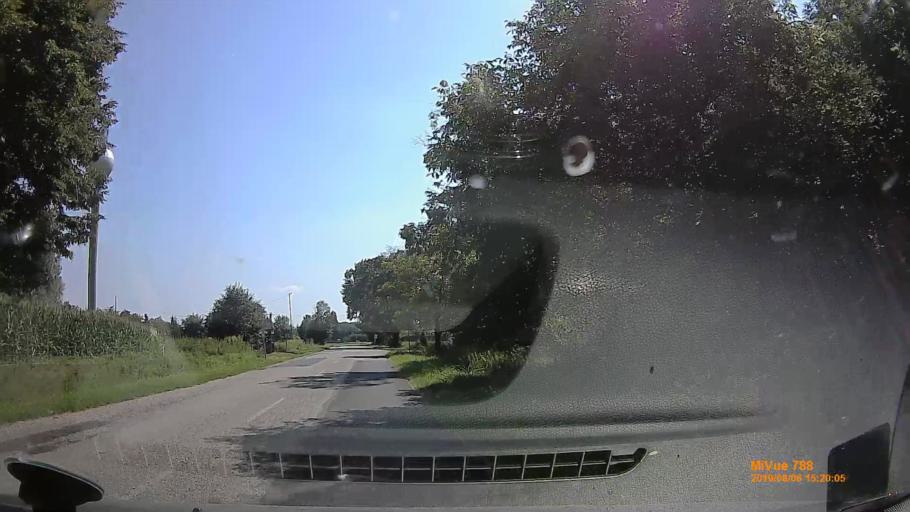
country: HR
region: Koprivnicko-Krizevacka
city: Drnje
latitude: 46.2873
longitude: 16.9482
